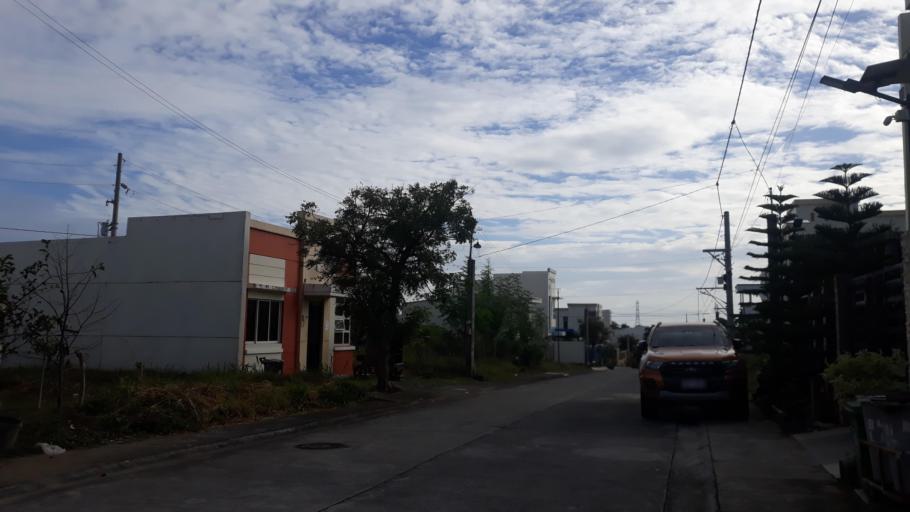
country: PH
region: Calabarzon
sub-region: Province of Cavite
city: Biga
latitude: 14.2730
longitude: 120.9678
